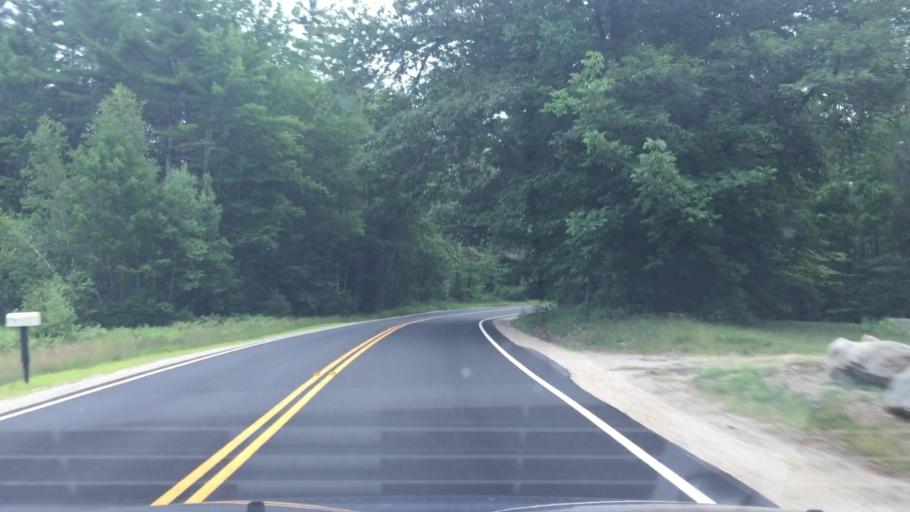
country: US
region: New Hampshire
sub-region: Carroll County
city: Freedom
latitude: 43.8431
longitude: -71.0837
